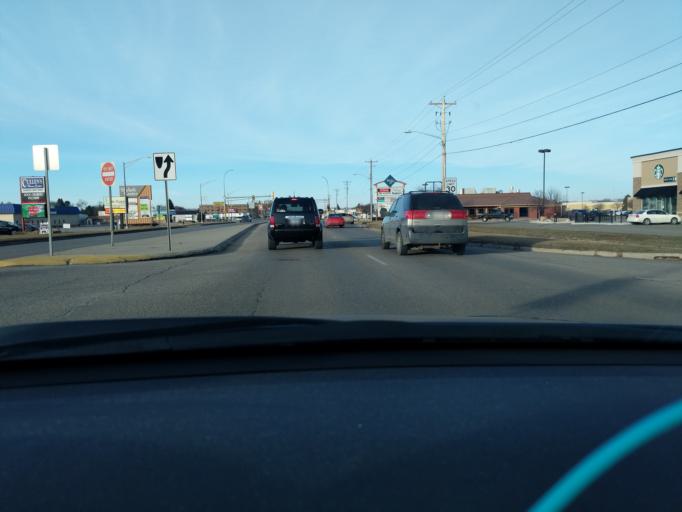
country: US
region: Minnesota
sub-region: Kandiyohi County
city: Willmar
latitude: 45.1044
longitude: -95.0426
